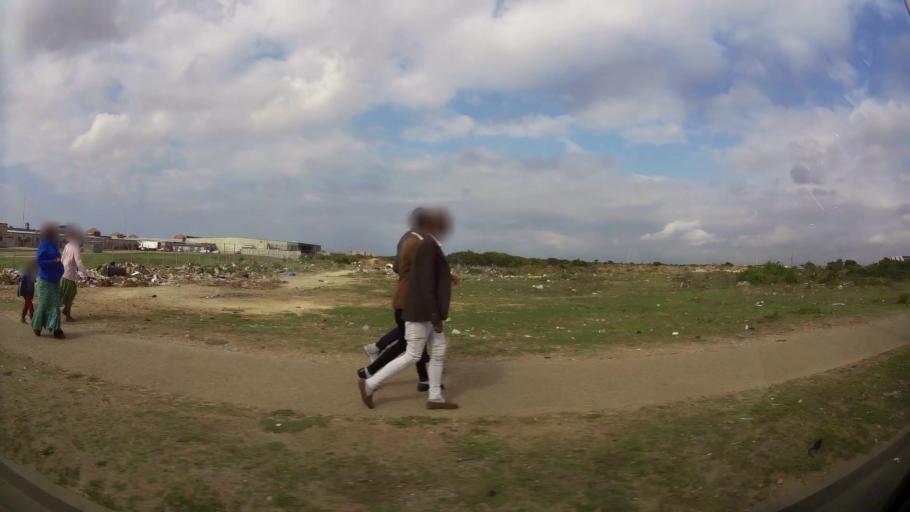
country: ZA
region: Eastern Cape
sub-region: Nelson Mandela Bay Metropolitan Municipality
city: Port Elizabeth
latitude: -33.8110
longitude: 25.5924
